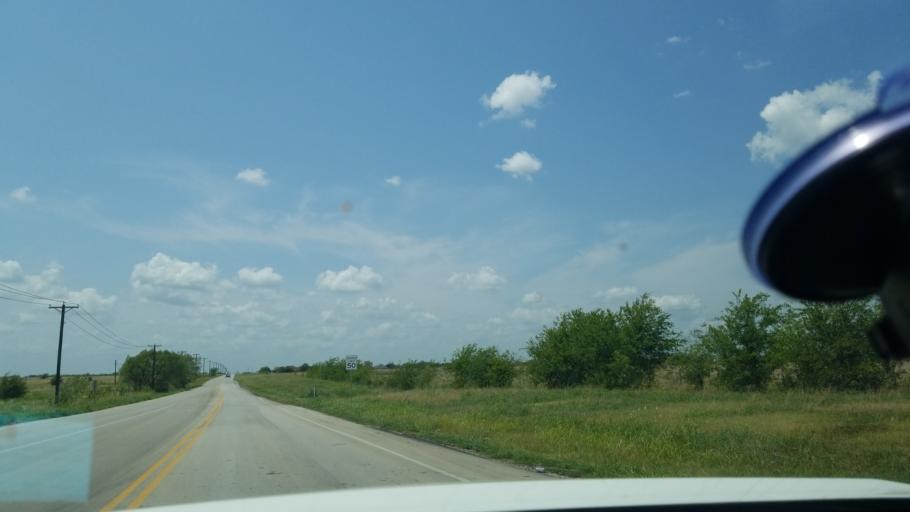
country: US
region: Texas
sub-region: Tarrant County
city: Eagle Mountain
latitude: 32.9244
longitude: -97.3928
